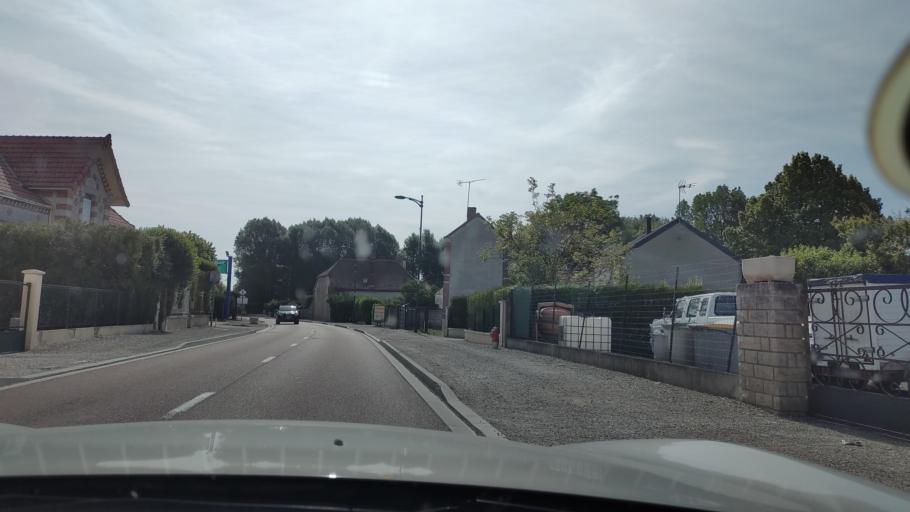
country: FR
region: Champagne-Ardenne
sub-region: Departement de l'Aube
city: Marigny-le-Chatel
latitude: 48.4019
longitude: 3.7442
